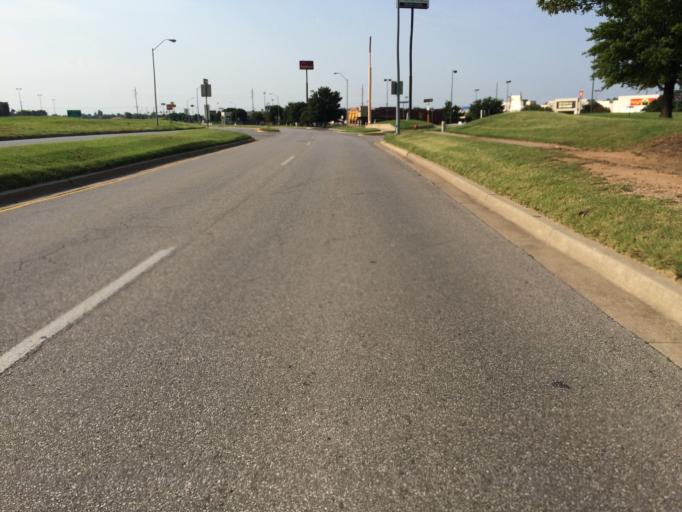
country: US
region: Oklahoma
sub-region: Cleveland County
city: Norman
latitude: 35.2148
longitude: -97.4859
